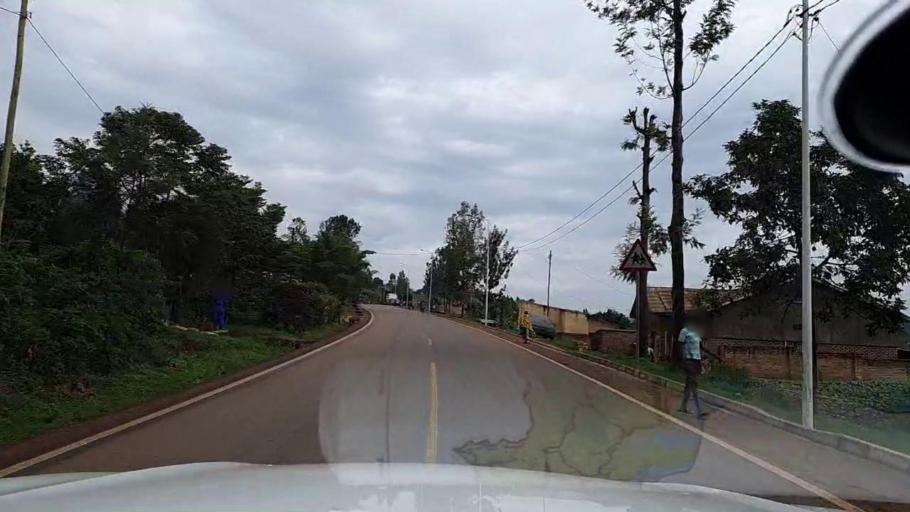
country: RW
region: Southern Province
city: Butare
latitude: -2.5811
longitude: 29.7358
